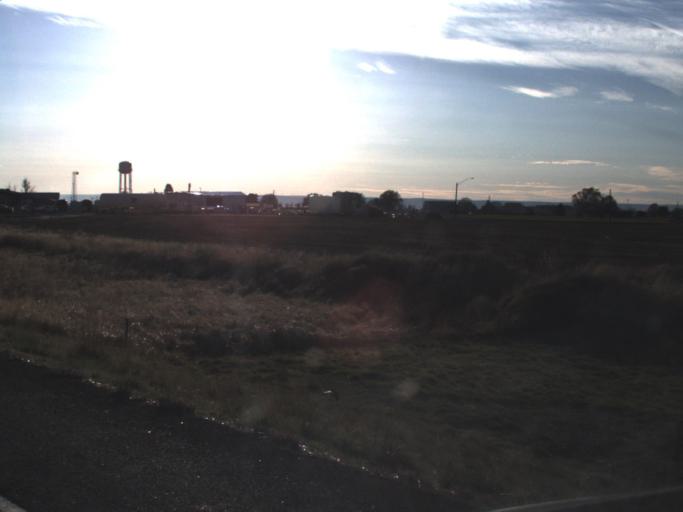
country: US
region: Washington
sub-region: Walla Walla County
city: Walla Walla East
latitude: 46.0954
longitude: -118.2554
